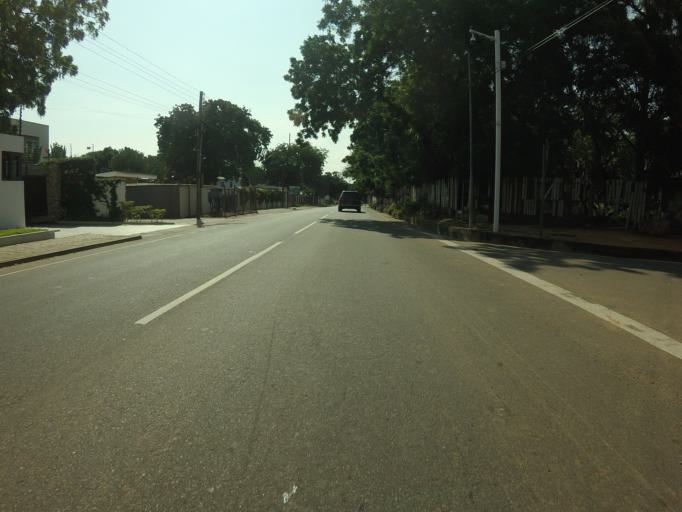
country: GH
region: Greater Accra
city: Accra
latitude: 5.5780
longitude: -0.1674
